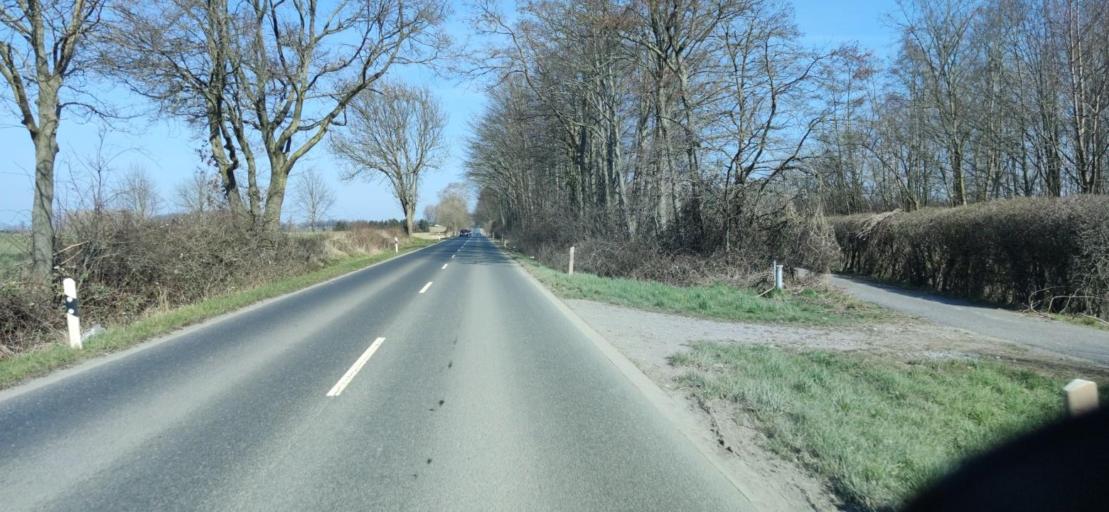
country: DE
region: North Rhine-Westphalia
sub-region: Regierungsbezirk Dusseldorf
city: Erkrath
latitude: 51.2465
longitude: 6.8951
